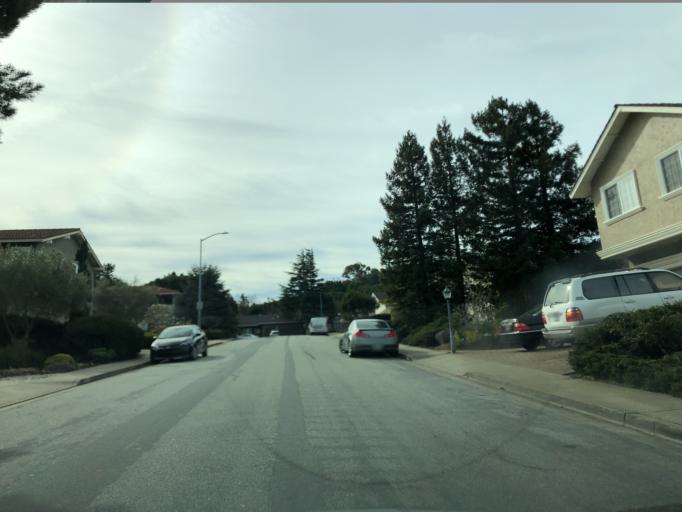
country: US
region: California
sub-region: San Mateo County
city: Belmont
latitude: 37.5040
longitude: -122.3077
